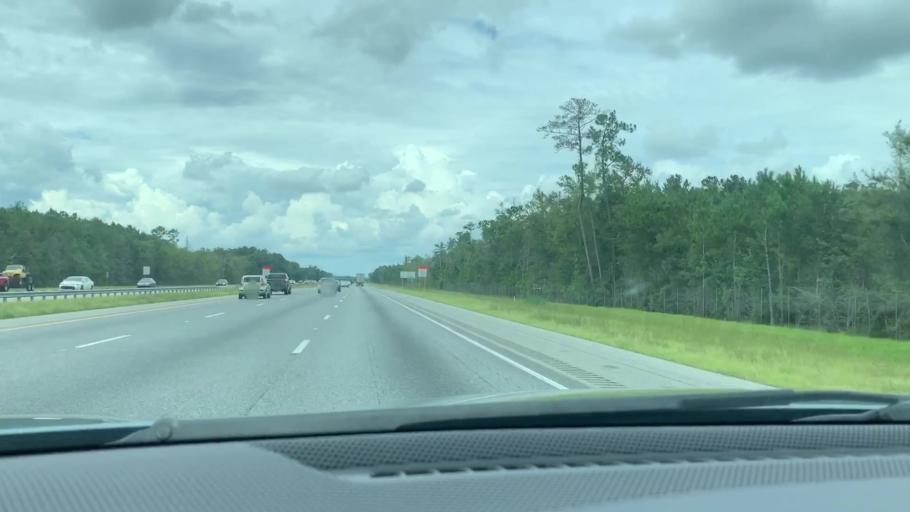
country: US
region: Georgia
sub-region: McIntosh County
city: Darien
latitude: 31.4551
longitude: -81.4455
